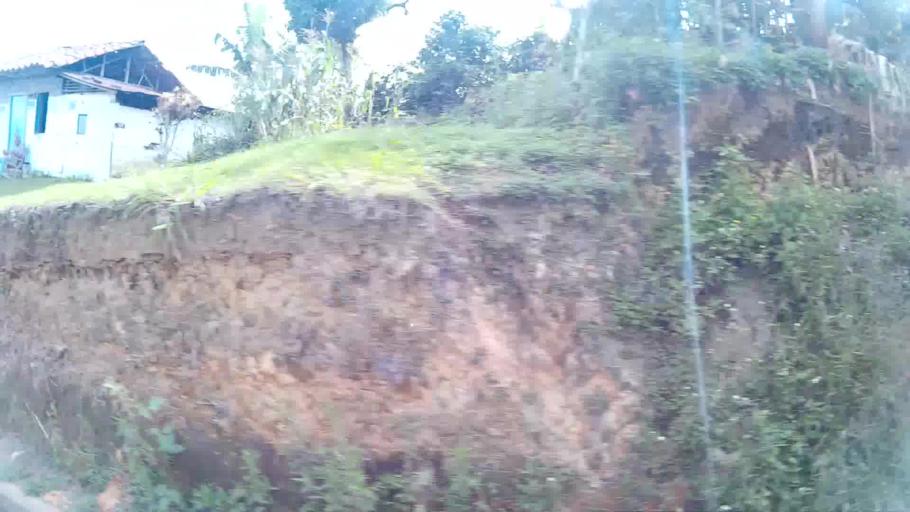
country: CO
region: Caldas
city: Belalcazar
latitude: 4.9836
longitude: -75.8144
